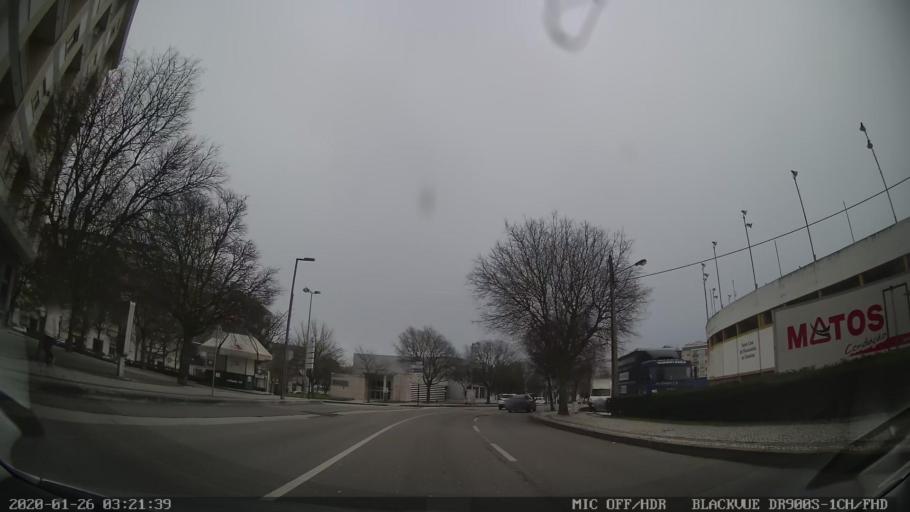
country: PT
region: Santarem
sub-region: Santarem
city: Santarem
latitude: 39.2290
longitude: -8.6874
